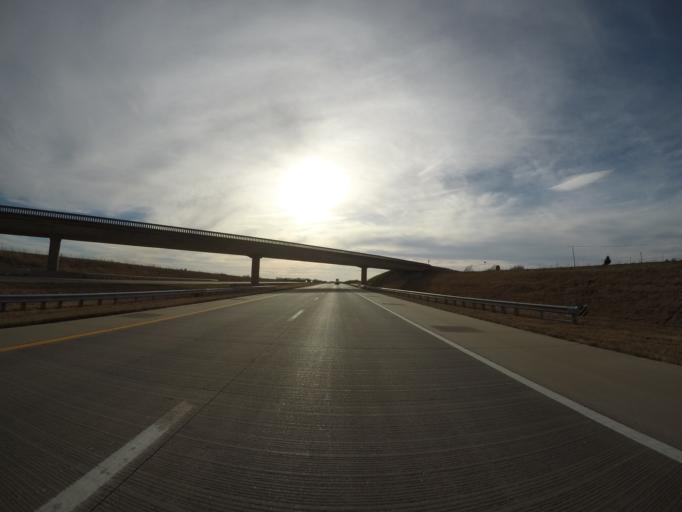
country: US
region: Kansas
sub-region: Franklin County
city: Ottawa
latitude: 38.6525
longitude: -95.1952
